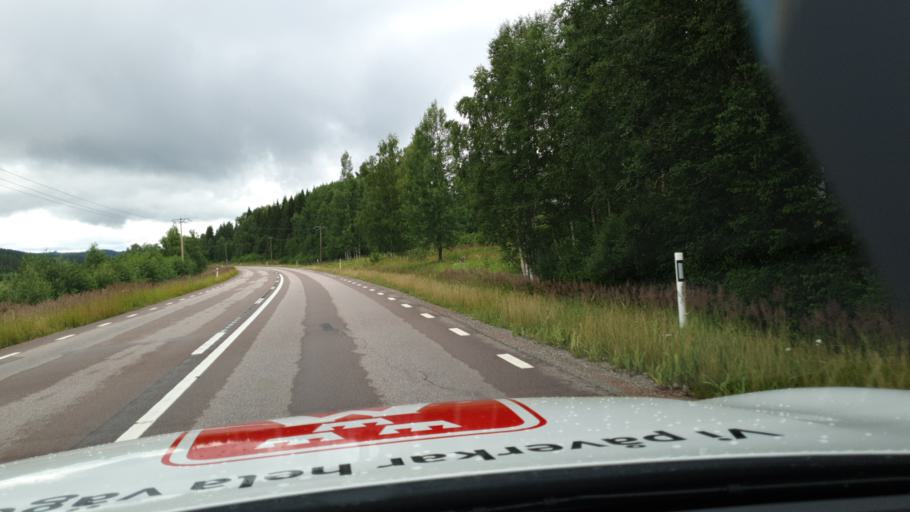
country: SE
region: Jaemtland
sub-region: Braecke Kommun
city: Braecke
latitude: 63.1602
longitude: 15.7407
